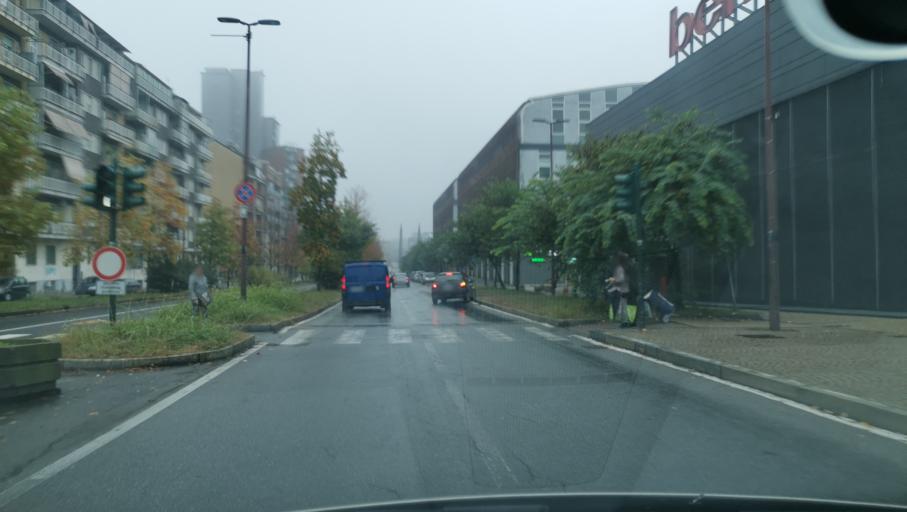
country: IT
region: Piedmont
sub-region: Provincia di Torino
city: Turin
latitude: 45.0937
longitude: 7.6710
